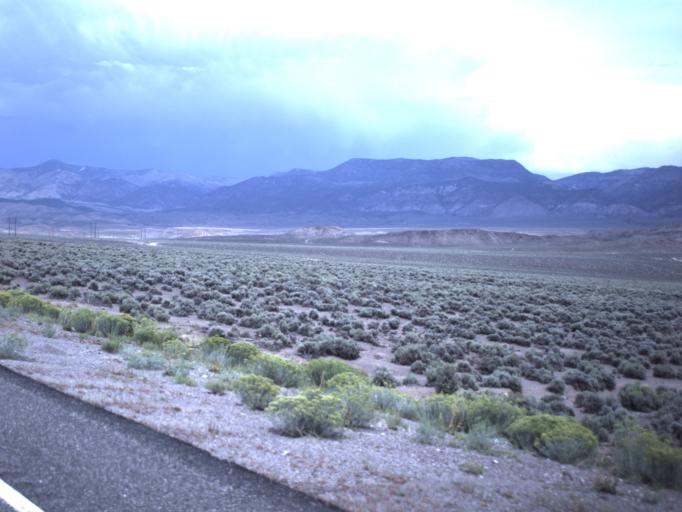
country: US
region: Utah
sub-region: Piute County
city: Junction
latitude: 38.3229
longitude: -112.2196
